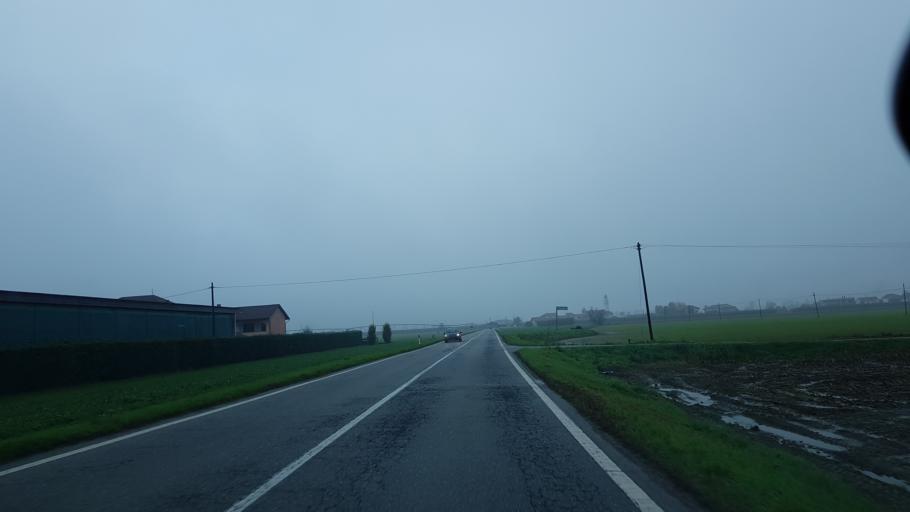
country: IT
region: Piedmont
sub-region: Provincia di Cuneo
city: Genola
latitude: 44.5573
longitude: 7.6646
